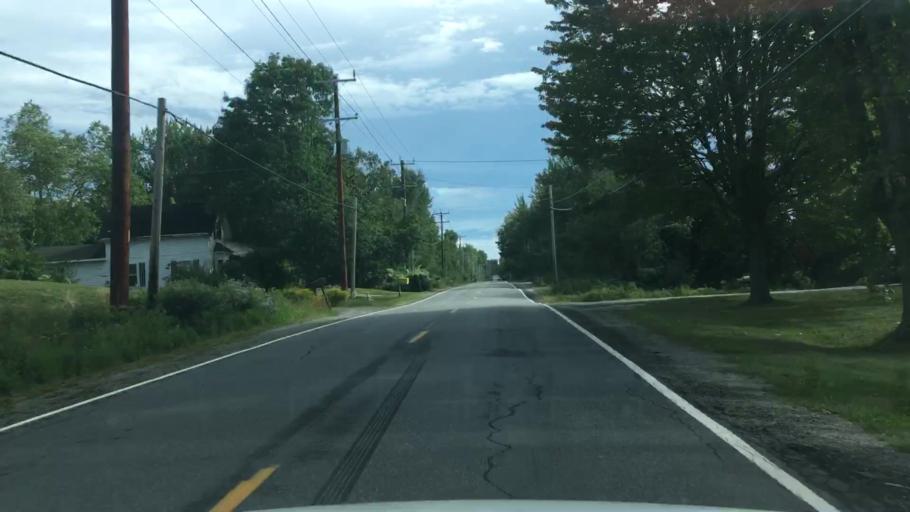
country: US
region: Maine
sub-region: Hancock County
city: Ellsworth
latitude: 44.4964
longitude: -68.4204
